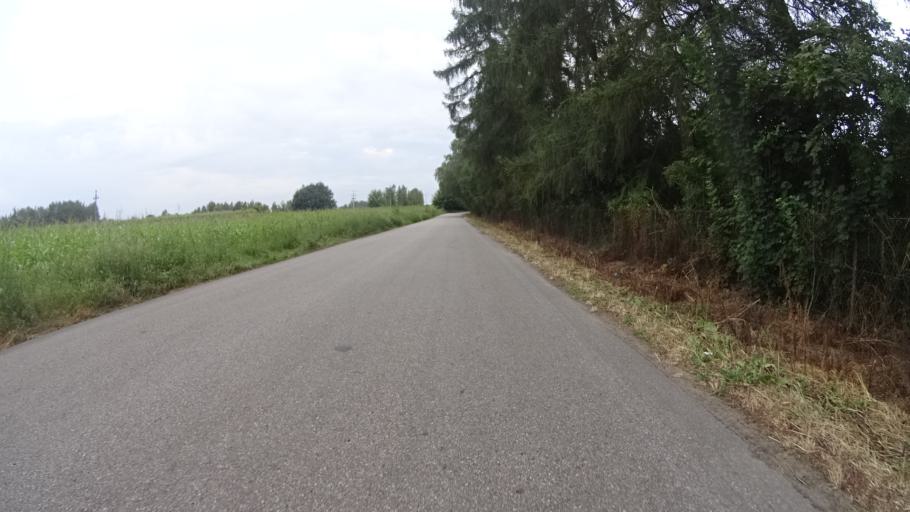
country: PL
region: Masovian Voivodeship
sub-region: Powiat grojecki
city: Goszczyn
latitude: 51.6864
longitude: 20.8610
